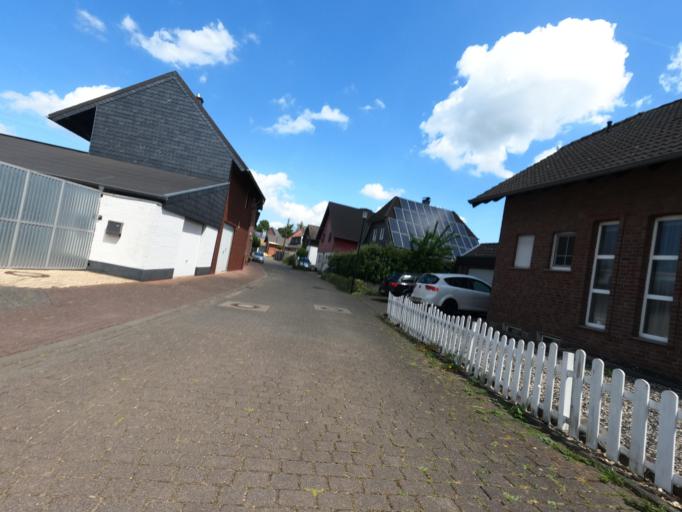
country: DE
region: North Rhine-Westphalia
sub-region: Regierungsbezirk Koln
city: Wassenberg
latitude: 51.0804
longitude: 6.1590
